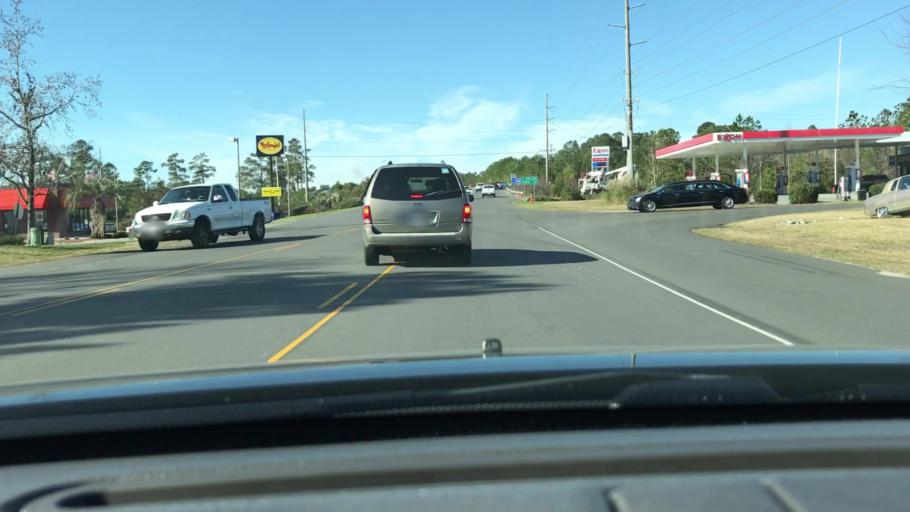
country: US
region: North Carolina
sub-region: Brunswick County
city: Shallotte
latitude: 33.9742
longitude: -78.4013
